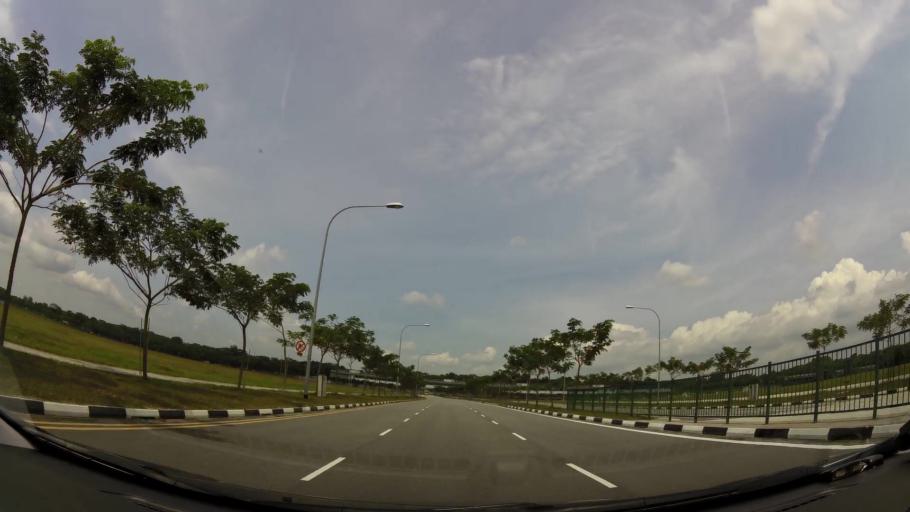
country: MY
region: Johor
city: Johor Bahru
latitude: 1.3574
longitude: 103.7080
